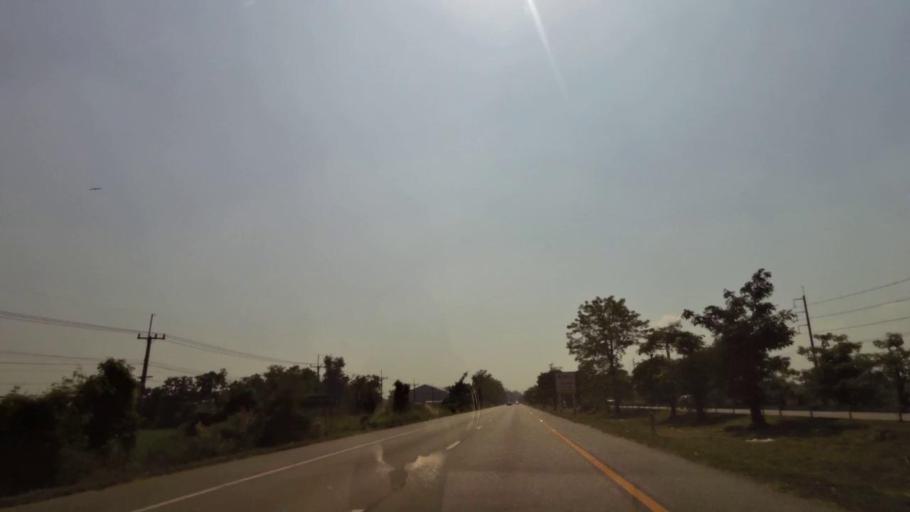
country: TH
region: Phichit
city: Wachira Barami
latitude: 16.6266
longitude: 100.1499
